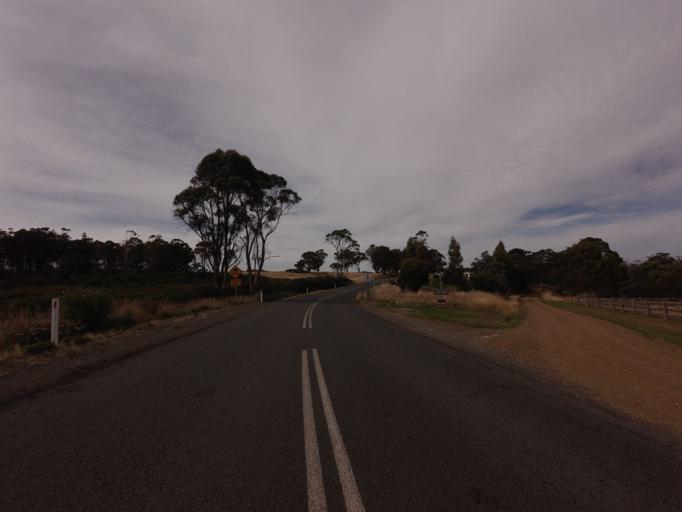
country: AU
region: Tasmania
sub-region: Sorell
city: Sorell
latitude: -42.4017
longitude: 147.4504
